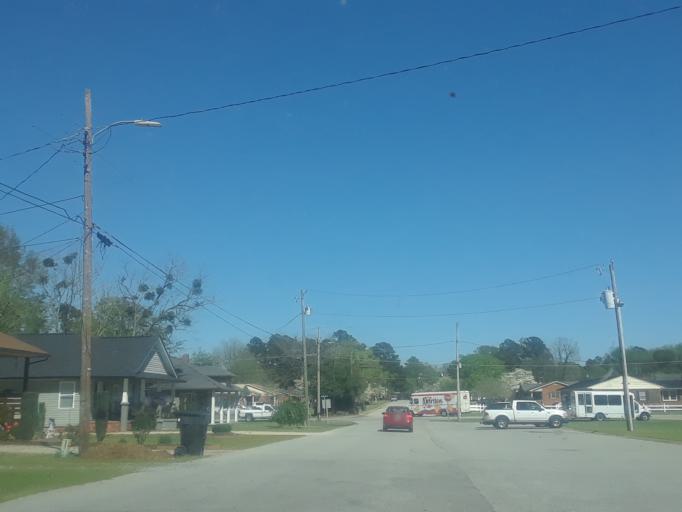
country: US
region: North Carolina
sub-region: Harnett County
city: Erwin
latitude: 35.3229
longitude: -78.6769
